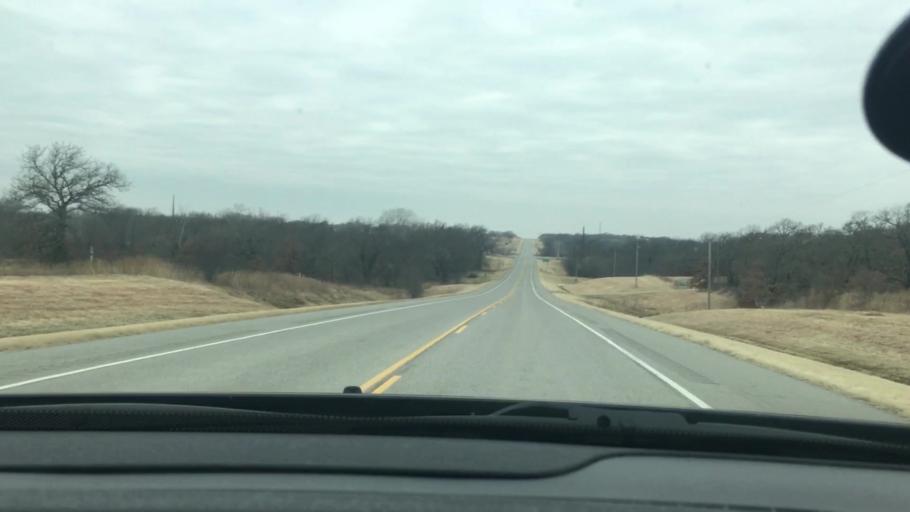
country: US
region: Oklahoma
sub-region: Carter County
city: Healdton
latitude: 34.4924
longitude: -97.3987
